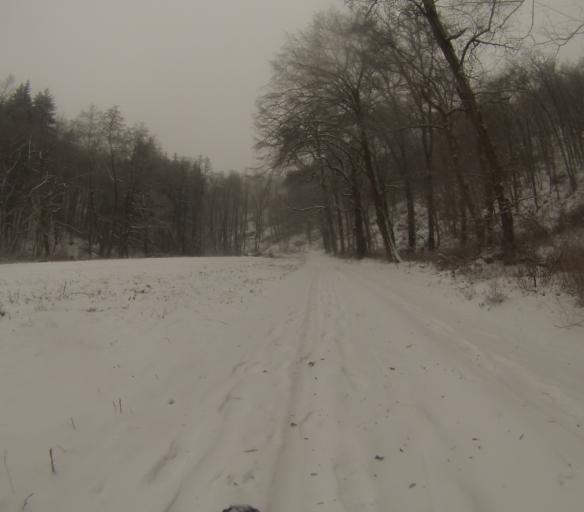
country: CZ
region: South Moravian
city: Strelice
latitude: 49.1355
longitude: 16.5127
